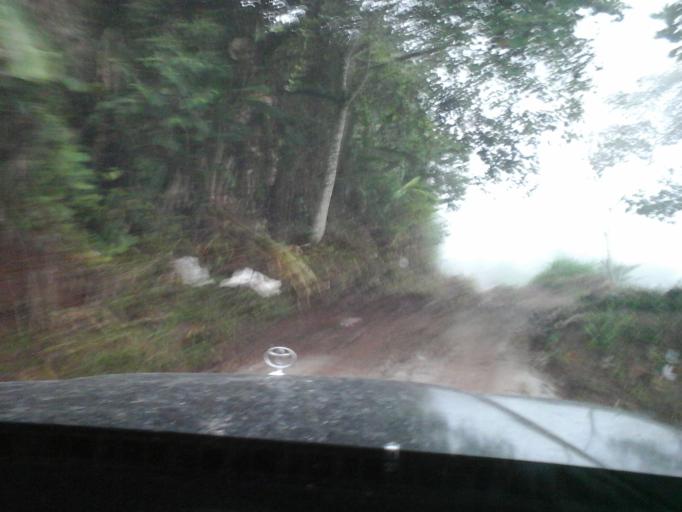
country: CO
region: Cesar
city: Agustin Codazzi
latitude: 9.9419
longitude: -73.1228
